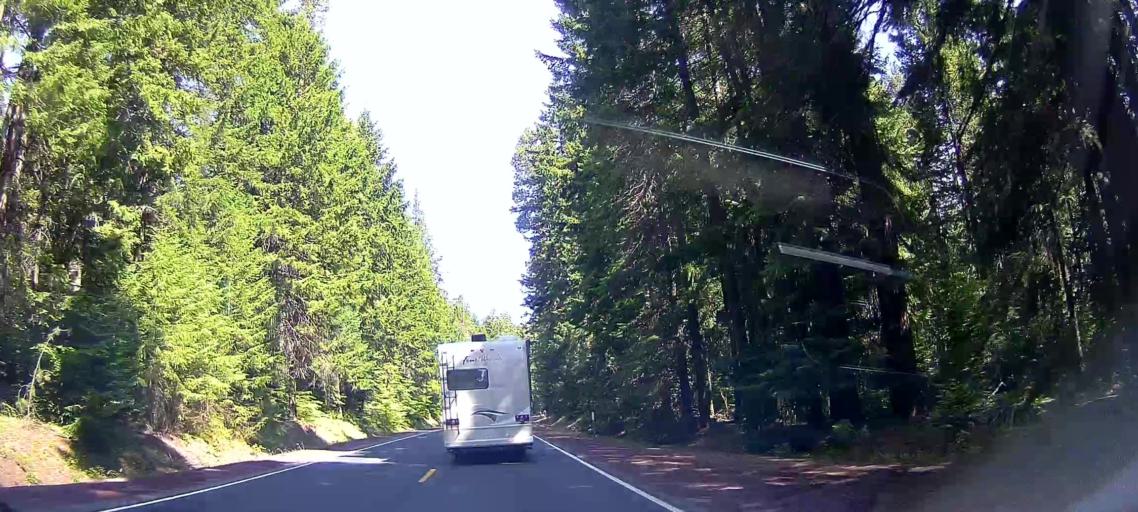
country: US
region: Oregon
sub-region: Jefferson County
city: Warm Springs
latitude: 45.0820
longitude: -121.5421
